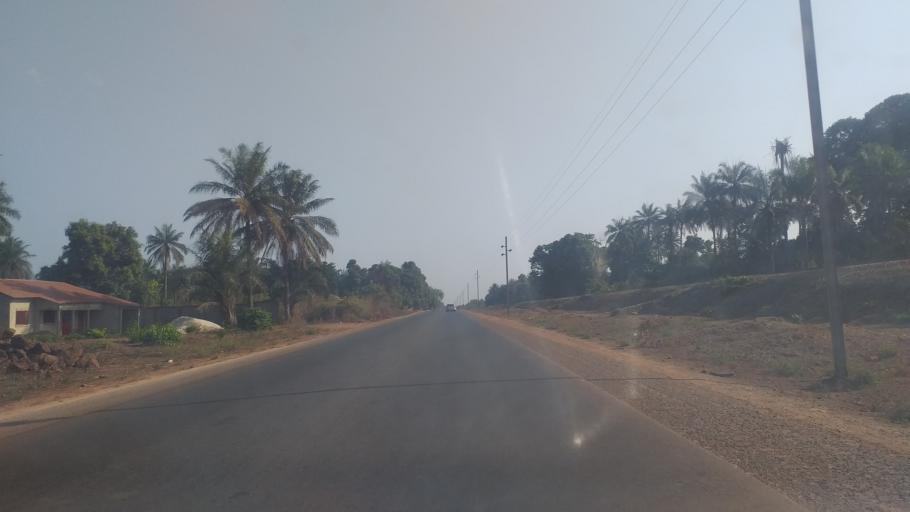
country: GN
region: Boke
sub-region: Boke Prefecture
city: Kamsar
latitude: 10.7141
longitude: -14.5226
